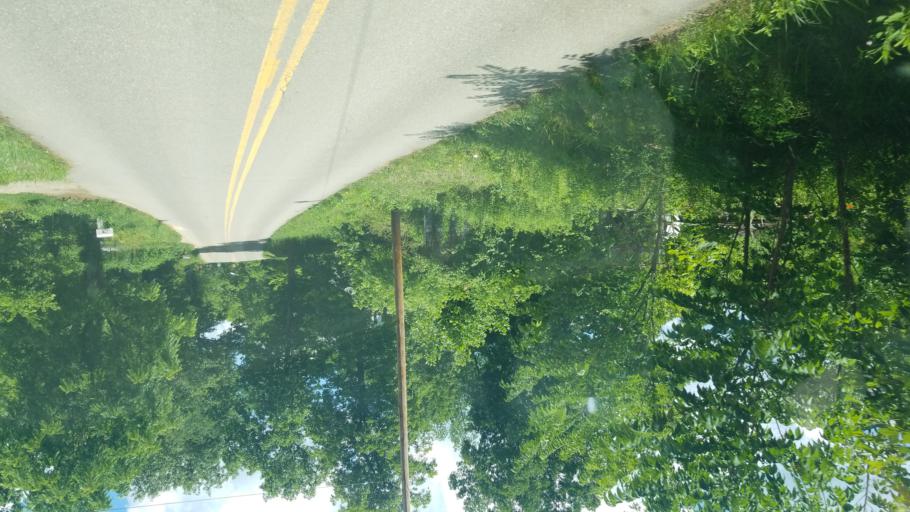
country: US
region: Ohio
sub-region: Gallia County
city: Gallipolis
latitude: 38.7314
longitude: -82.3679
